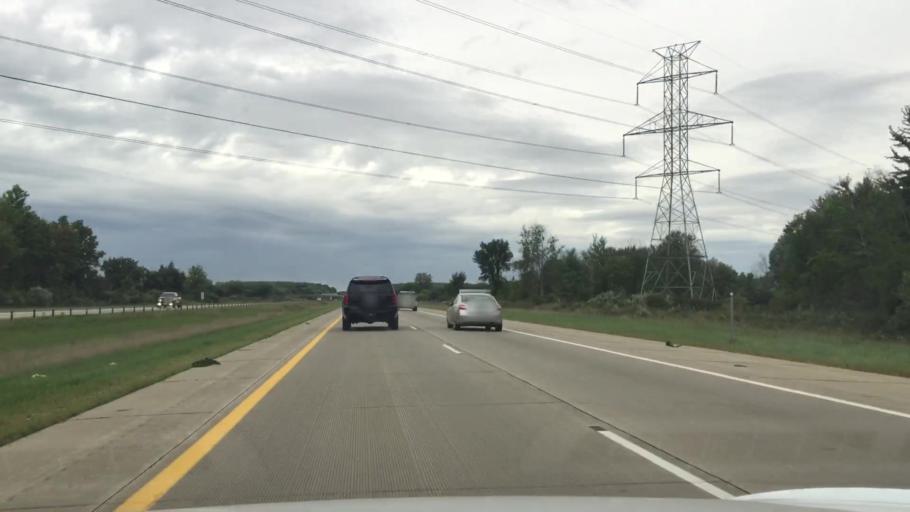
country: US
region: Michigan
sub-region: Macomb County
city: Richmond
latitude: 42.7714
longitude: -82.6842
